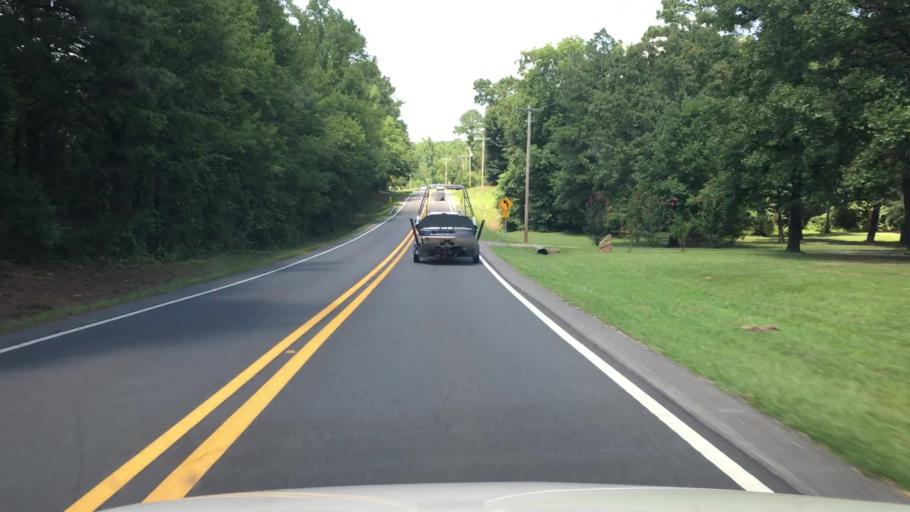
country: US
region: Arkansas
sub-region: Garland County
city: Lake Hamilton
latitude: 34.2918
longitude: -93.1632
